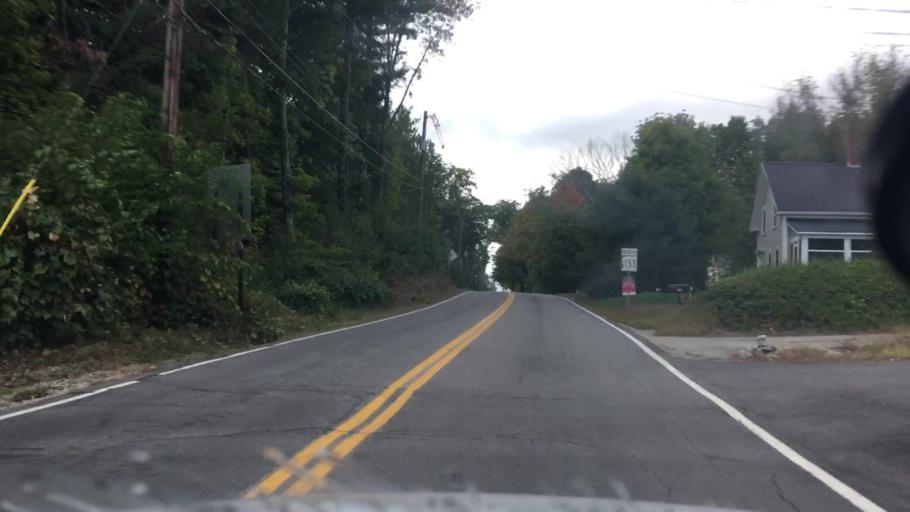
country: US
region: New Hampshire
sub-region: Carroll County
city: Sanbornville
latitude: 43.5544
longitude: -71.0267
